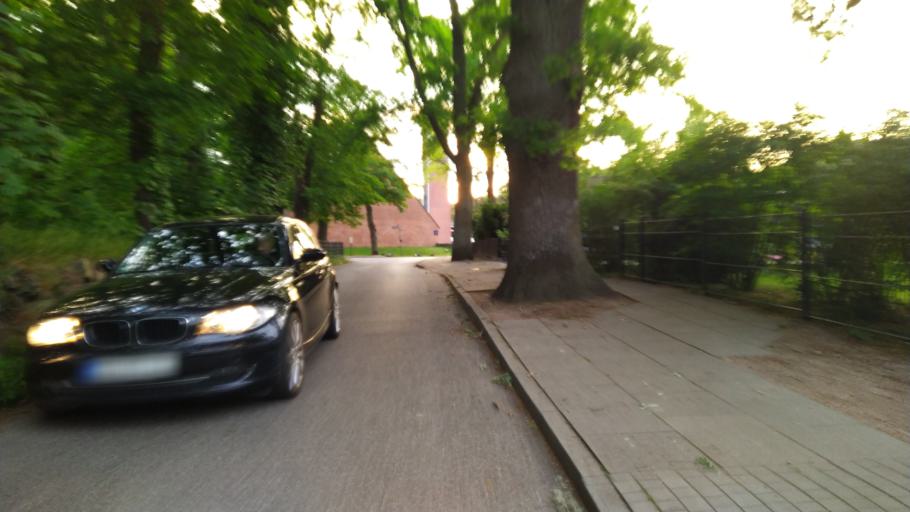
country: DE
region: Lower Saxony
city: Neu Wulmstorf
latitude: 53.4731
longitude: 9.8297
